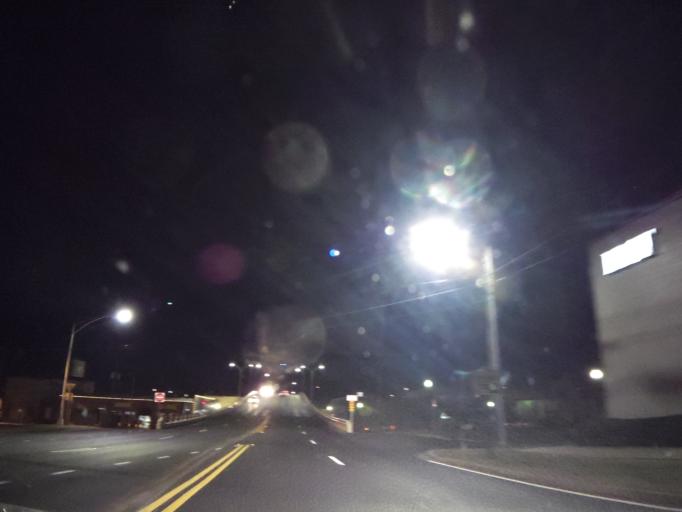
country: US
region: Georgia
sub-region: Whitfield County
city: Dalton
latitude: 34.7742
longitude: -84.9696
